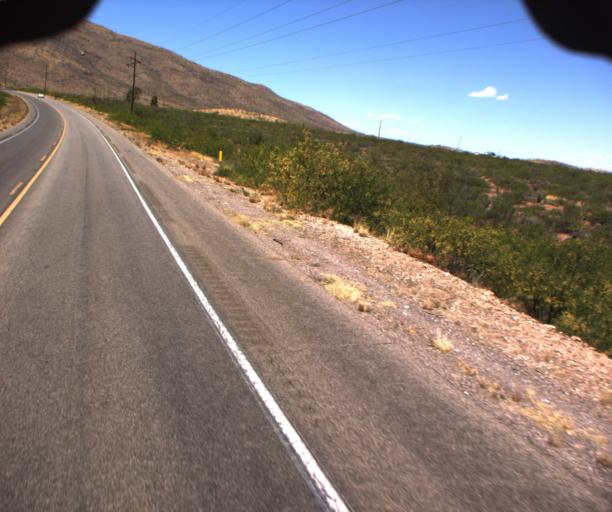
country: US
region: Arizona
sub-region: Cochise County
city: Bisbee
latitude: 31.4380
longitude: -109.8188
